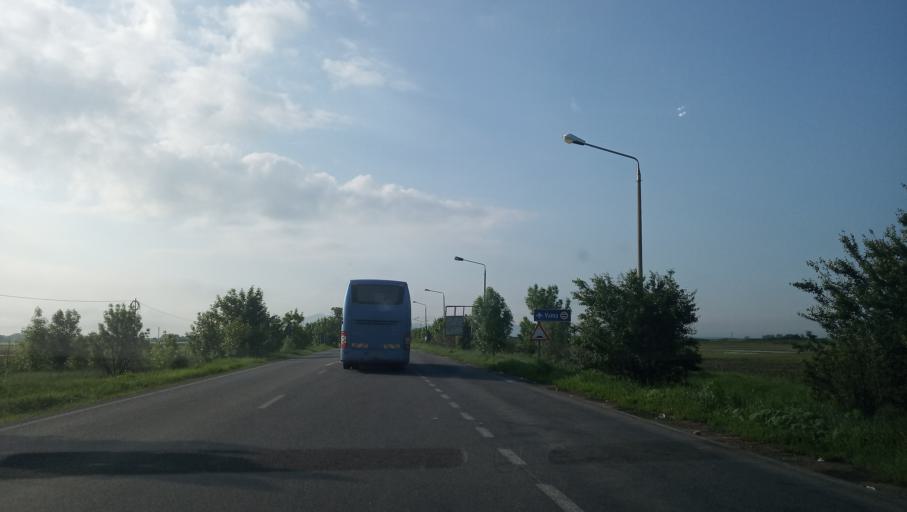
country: RO
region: Timis
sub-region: Comuna Moravita
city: Moravita
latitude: 45.2366
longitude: 21.2687
